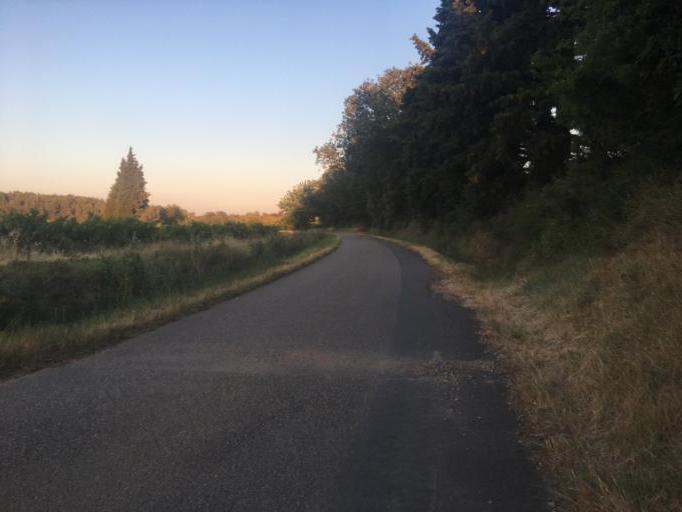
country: FR
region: Languedoc-Roussillon
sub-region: Departement du Gard
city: Saze
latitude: 43.9399
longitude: 4.6889
